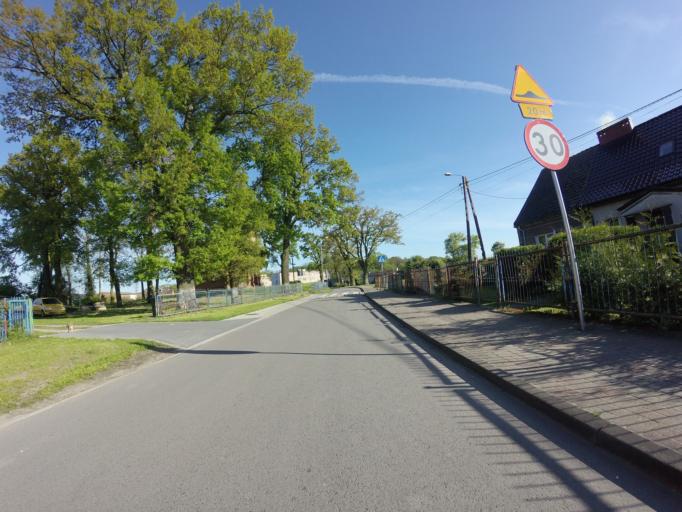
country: PL
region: West Pomeranian Voivodeship
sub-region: Powiat choszczenski
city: Pelczyce
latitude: 53.1185
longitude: 15.3223
